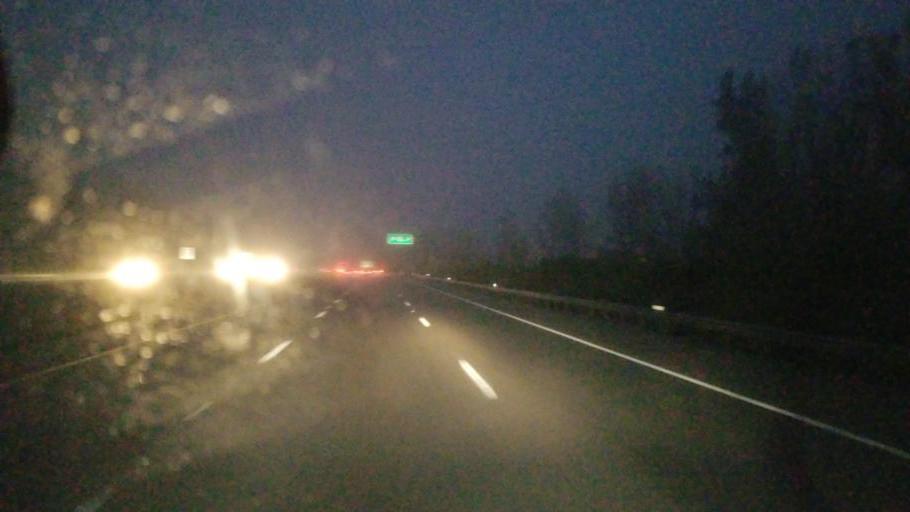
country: US
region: Ohio
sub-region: Ross County
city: Chillicothe
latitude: 39.3310
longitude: -82.9469
